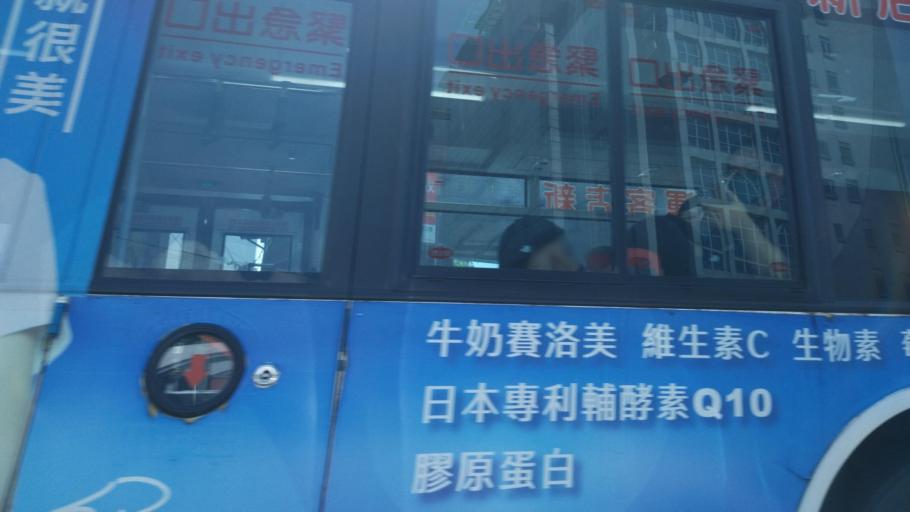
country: TW
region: Taipei
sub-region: Taipei
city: Banqiao
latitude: 24.9542
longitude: 121.5047
